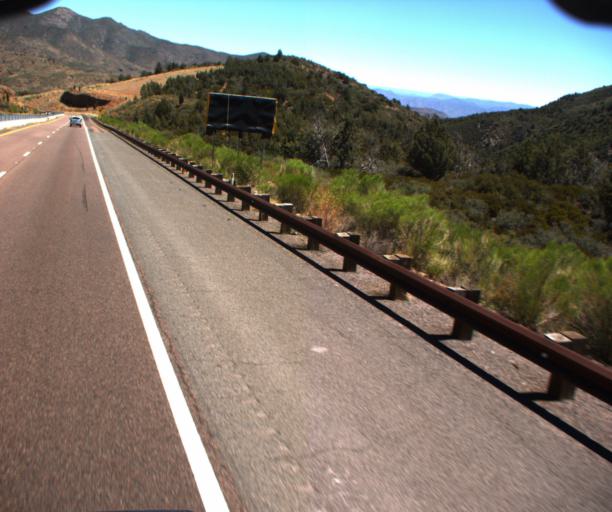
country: US
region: Arizona
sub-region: Gila County
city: Tonto Basin
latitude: 33.9329
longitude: -111.4417
